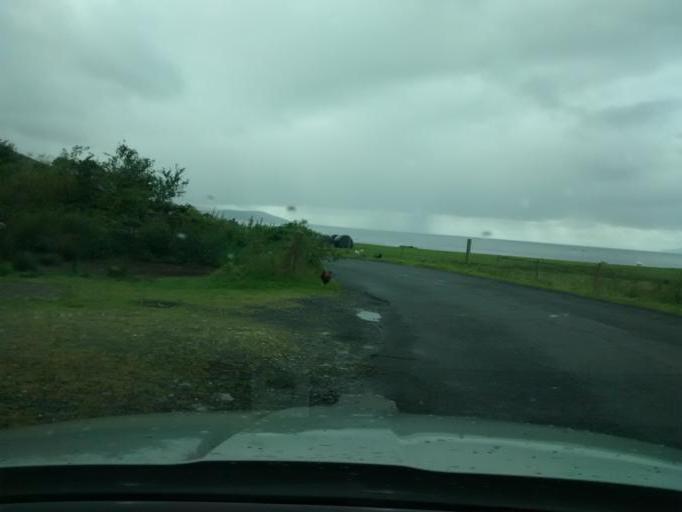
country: GB
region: Scotland
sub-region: North Ayrshire
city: Isle of Arran
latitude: 55.6115
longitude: -5.3919
